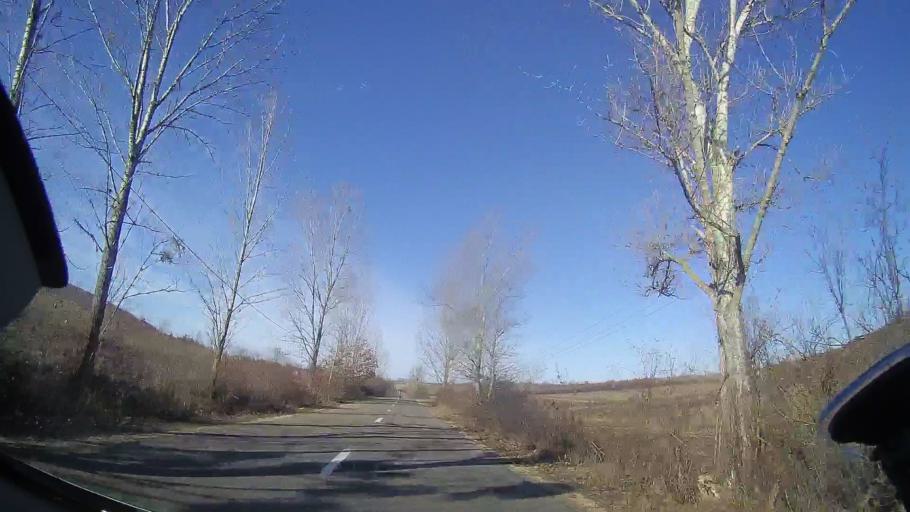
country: RO
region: Bihor
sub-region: Comuna Suncuius
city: Balnaca
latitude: 46.9660
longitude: 22.5514
